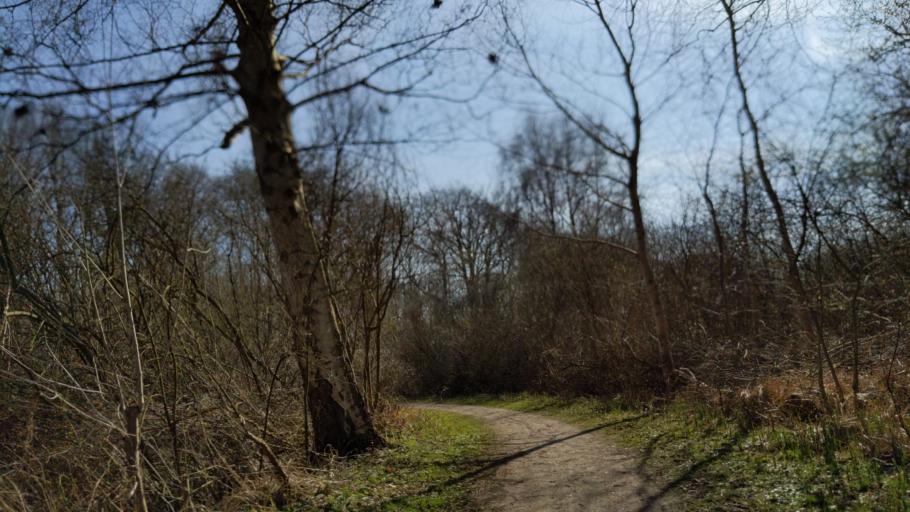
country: DE
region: Schleswig-Holstein
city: Timmendorfer Strand
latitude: 53.9874
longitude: 10.8209
